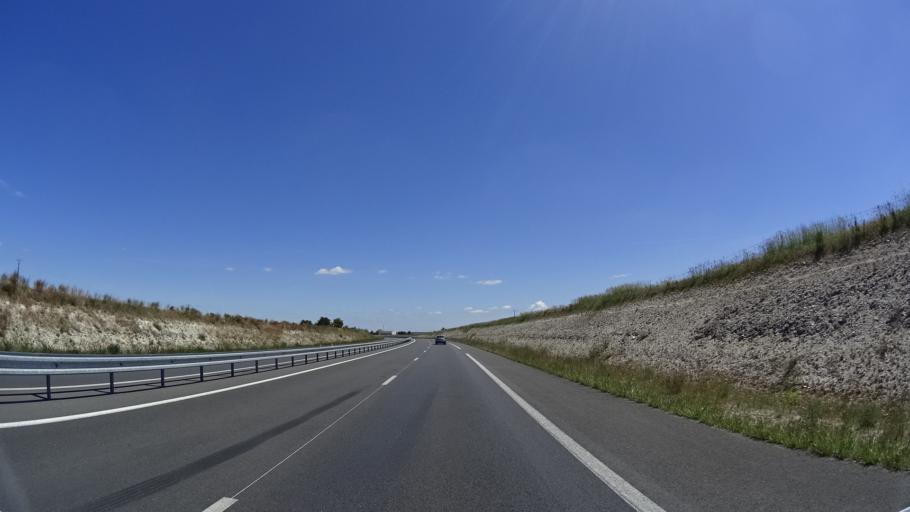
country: FR
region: Pays de la Loire
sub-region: Departement de Maine-et-Loire
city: Vaudelnay
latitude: 47.2069
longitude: -0.1944
